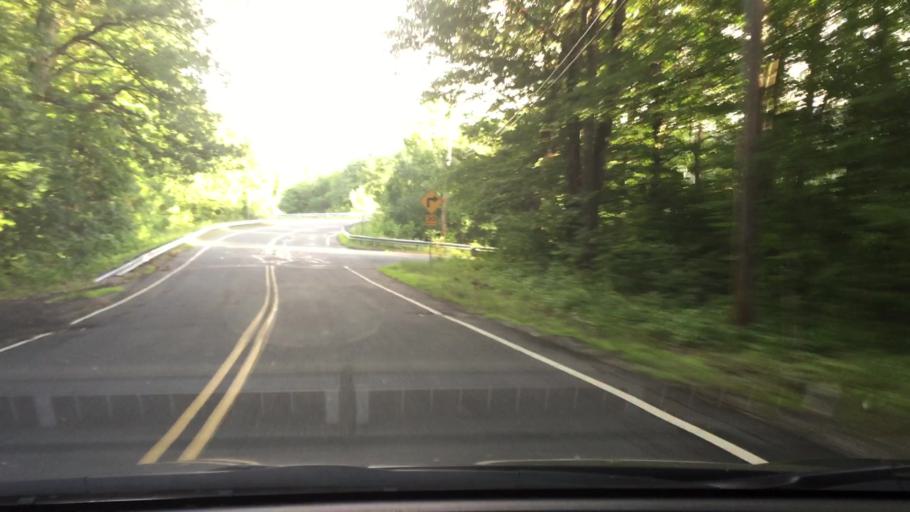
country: US
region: Massachusetts
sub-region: Hampden County
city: Westfield
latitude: 42.1917
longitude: -72.8485
